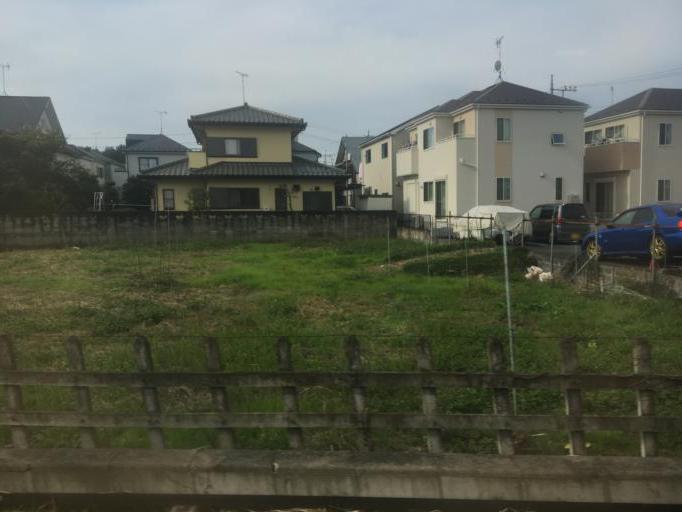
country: JP
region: Saitama
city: Sayama
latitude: 35.8334
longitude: 139.4097
